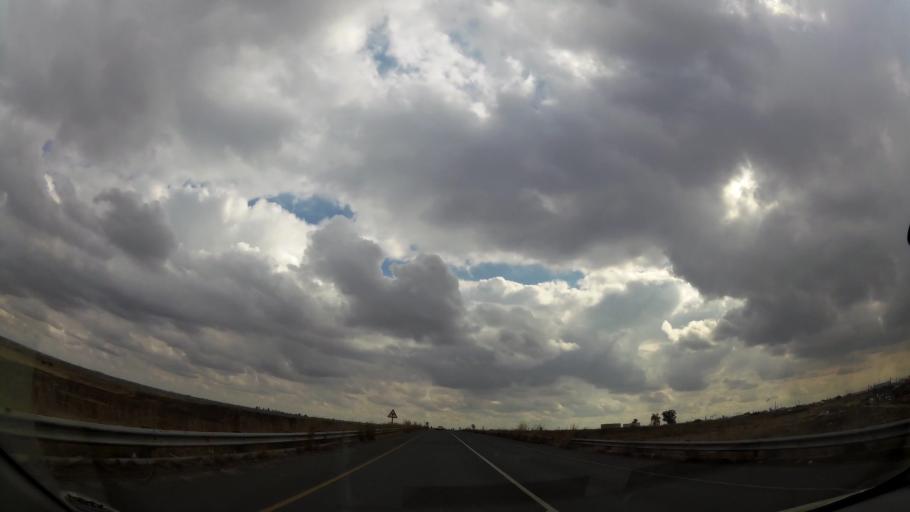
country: ZA
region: Orange Free State
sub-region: Fezile Dabi District Municipality
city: Sasolburg
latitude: -26.8656
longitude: 27.8878
